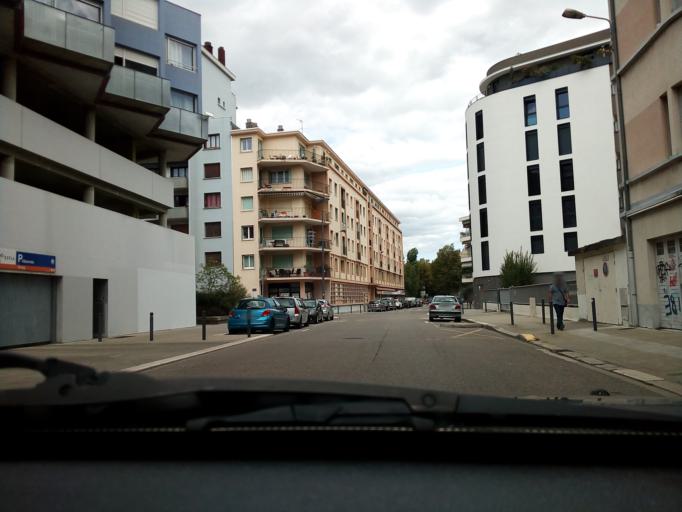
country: FR
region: Rhone-Alpes
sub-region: Departement de l'Isere
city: Grenoble
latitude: 45.1812
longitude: 5.7140
